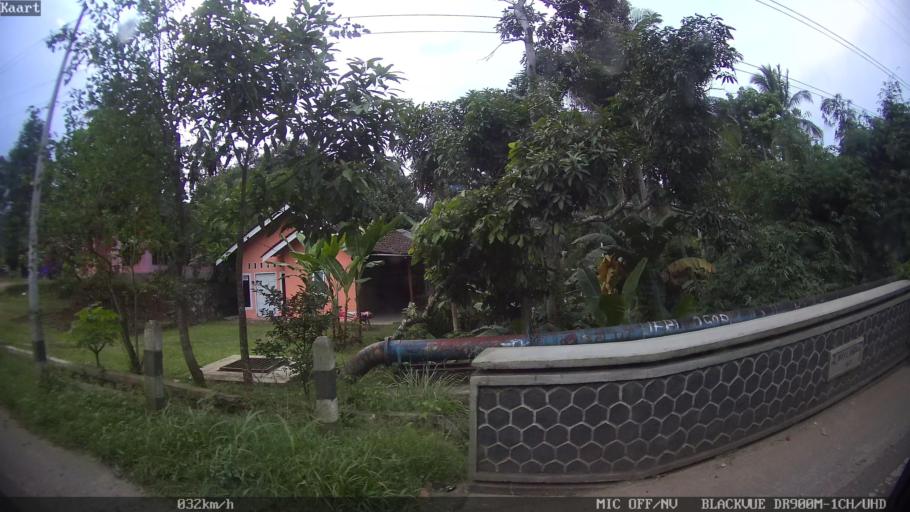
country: ID
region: Lampung
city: Gedongtataan
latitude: -5.3676
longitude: 105.1564
